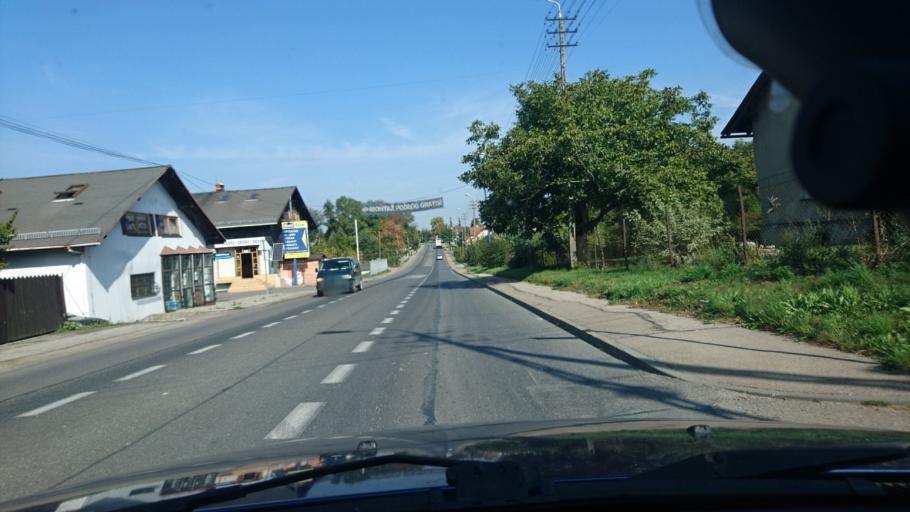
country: PL
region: Silesian Voivodeship
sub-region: Powiat bielski
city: Bestwina
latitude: 49.8806
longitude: 19.0264
